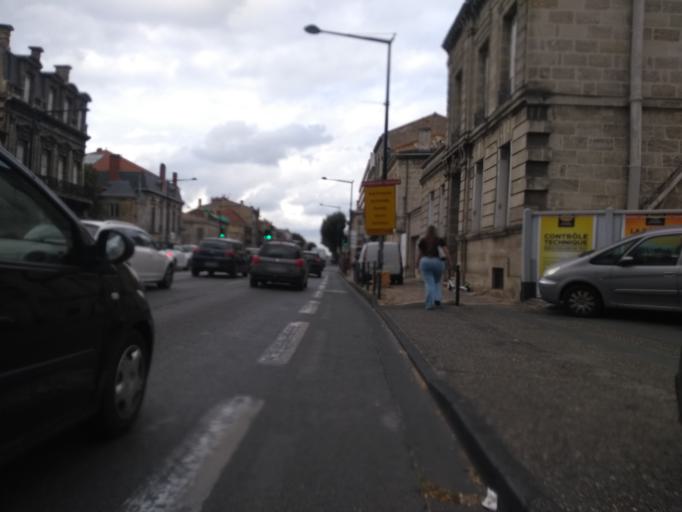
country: FR
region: Aquitaine
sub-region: Departement de la Gironde
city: Bordeaux
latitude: 44.8249
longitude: -0.5885
